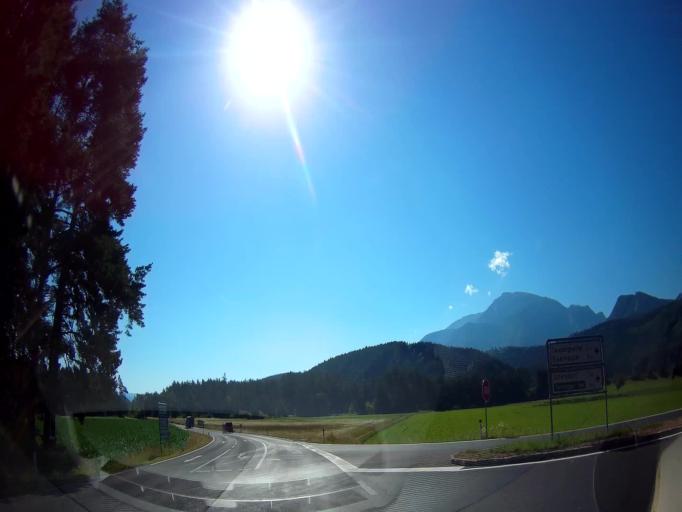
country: AT
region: Carinthia
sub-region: Politischer Bezirk Volkermarkt
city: Globasnitz
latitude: 46.5666
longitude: 14.6742
